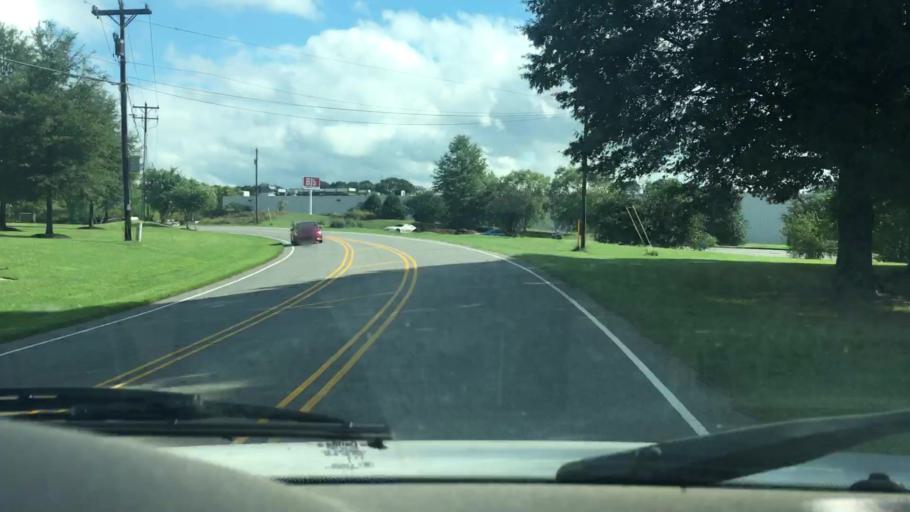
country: US
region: North Carolina
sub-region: Iredell County
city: Mooresville
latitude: 35.5986
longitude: -80.8638
